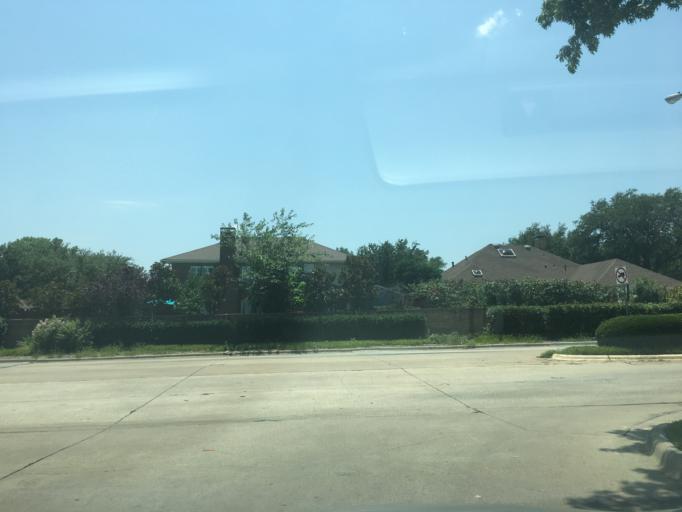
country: US
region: Texas
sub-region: Dallas County
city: Carrollton
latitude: 32.9491
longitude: -96.8634
